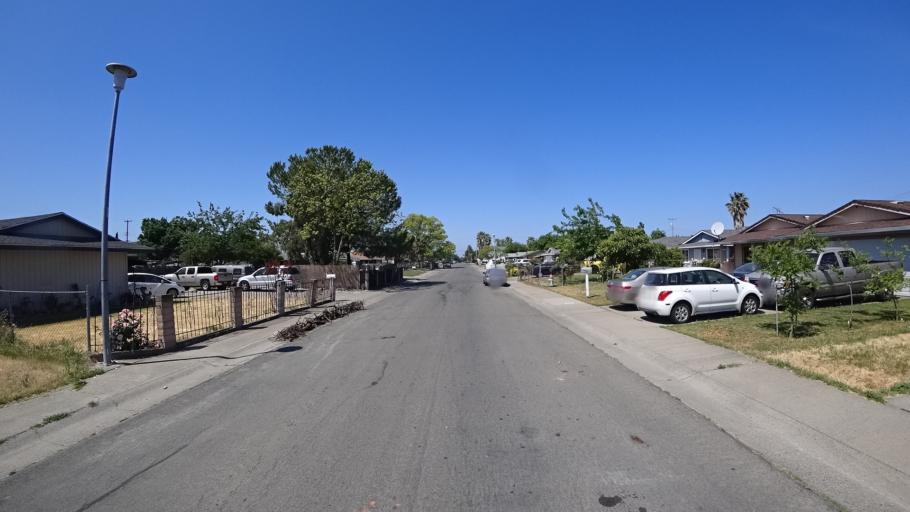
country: US
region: California
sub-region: Sacramento County
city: Parkway
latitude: 38.5057
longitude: -121.4770
